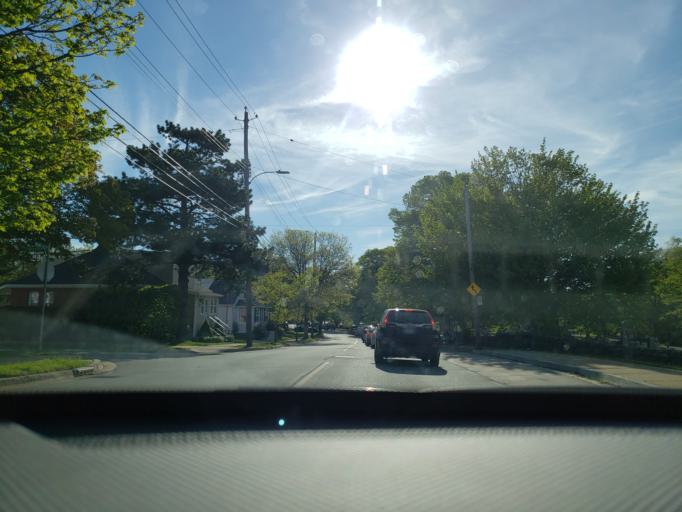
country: CA
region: Nova Scotia
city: Dartmouth
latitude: 44.6491
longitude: -63.6272
